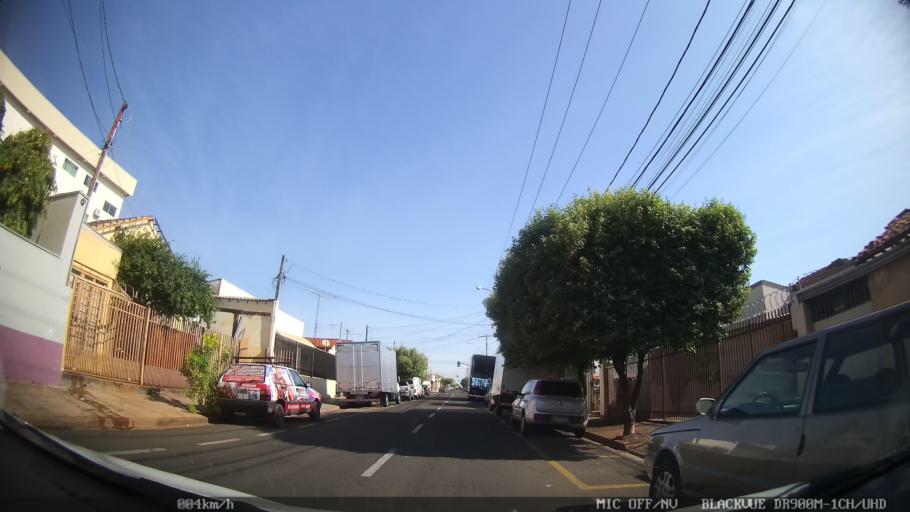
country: BR
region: Sao Paulo
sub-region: Sao Jose Do Rio Preto
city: Sao Jose do Rio Preto
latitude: -20.8028
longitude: -49.3920
